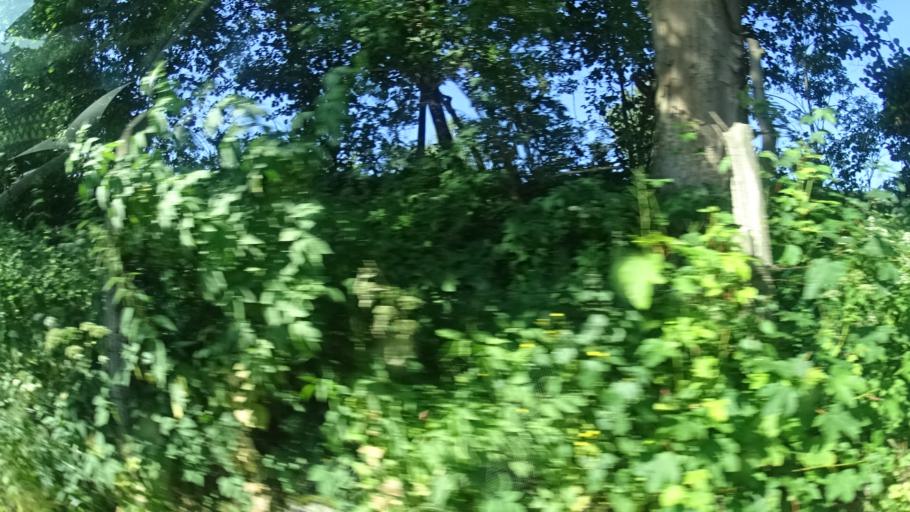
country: DE
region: Lower Saxony
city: Baddeckenstedt
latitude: 52.0845
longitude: 10.2302
